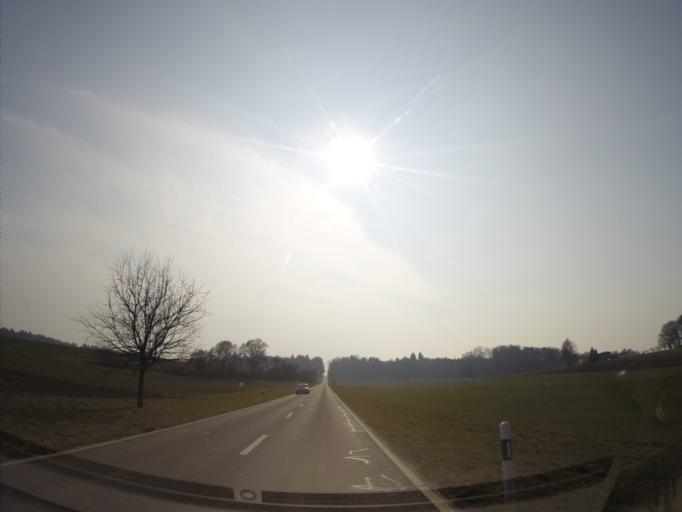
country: CH
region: Thurgau
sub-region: Frauenfeld District
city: Diessenhofen
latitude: 47.6576
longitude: 8.7325
